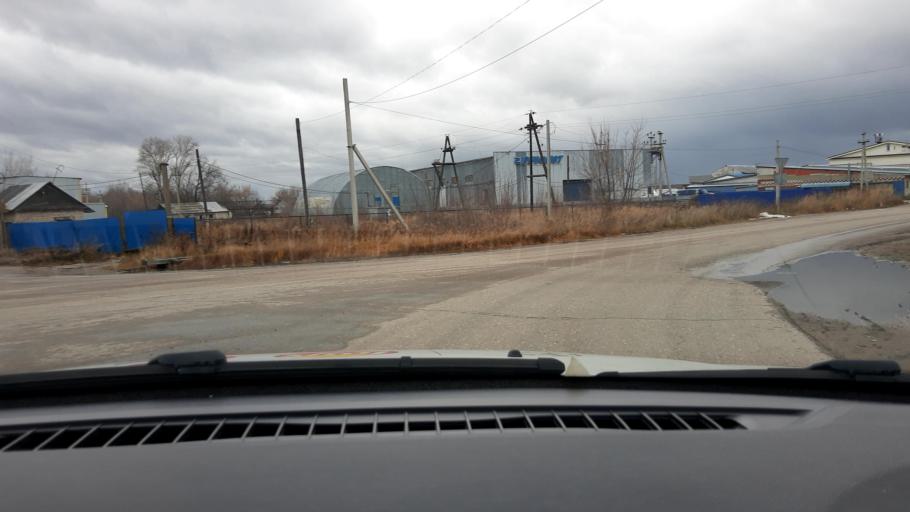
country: RU
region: Nizjnij Novgorod
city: Bogorodsk
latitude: 56.1155
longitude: 43.5278
